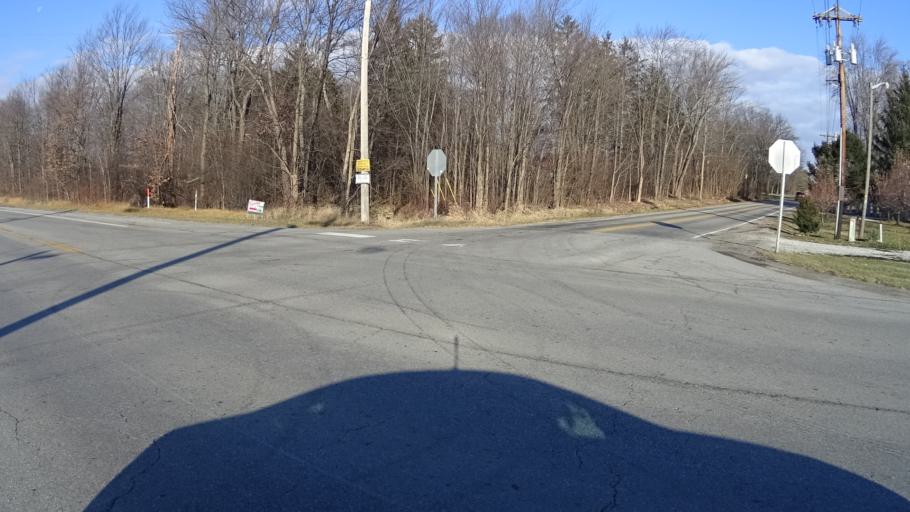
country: US
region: Ohio
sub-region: Lorain County
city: Oberlin
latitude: 41.2650
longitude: -82.2561
